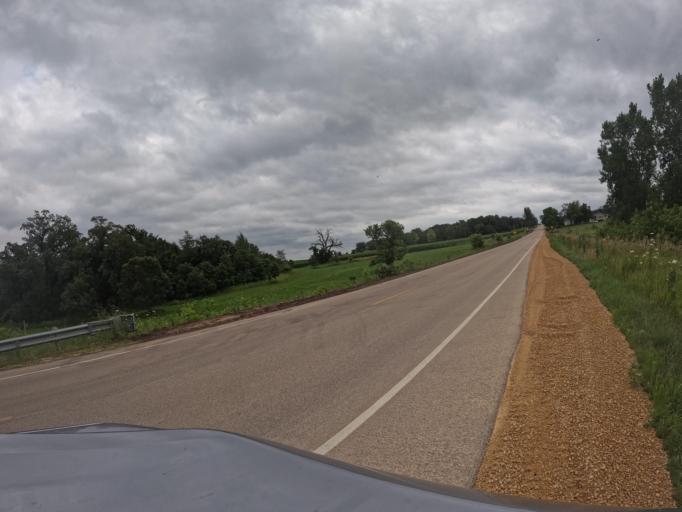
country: US
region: Iowa
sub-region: Clinton County
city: De Witt
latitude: 41.8031
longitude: -90.5102
